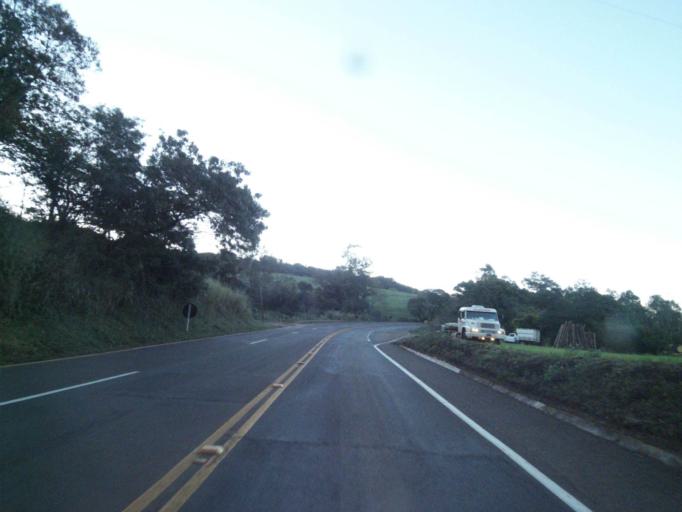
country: BR
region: Parana
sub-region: Apucarana
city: Apucarana
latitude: -23.6773
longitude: -51.1196
